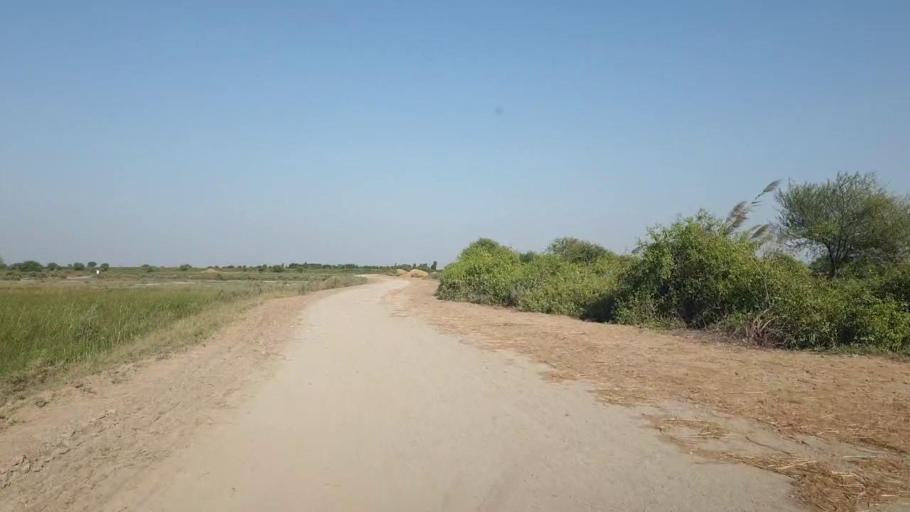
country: PK
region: Sindh
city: Rajo Khanani
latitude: 25.0082
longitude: 68.7722
